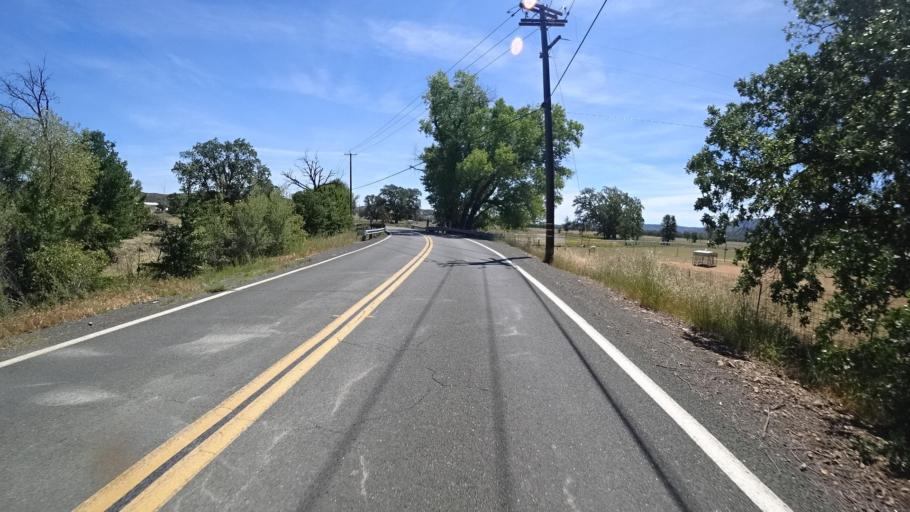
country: US
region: California
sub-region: Lake County
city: Middletown
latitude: 38.7459
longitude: -122.5831
